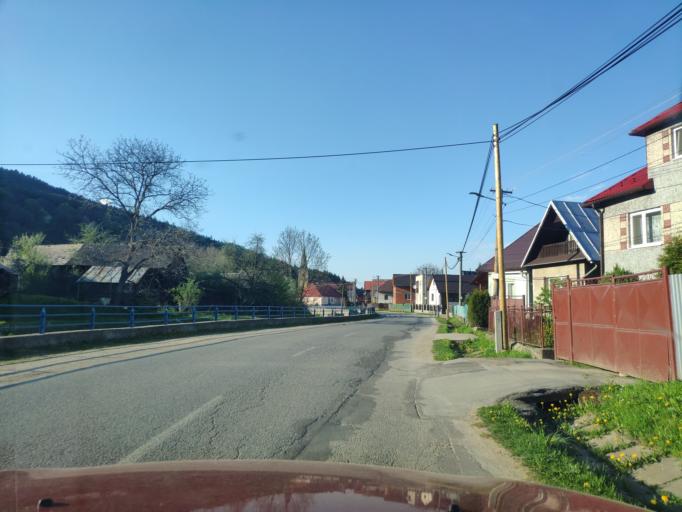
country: SK
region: Presovsky
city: Lipany
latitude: 49.1009
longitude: 20.8496
